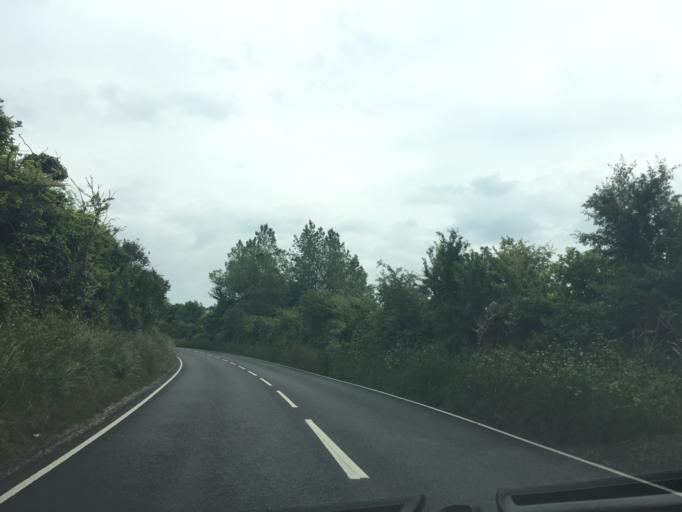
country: GB
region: England
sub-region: Dorset
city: Overcombe
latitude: 50.6462
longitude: -2.4153
